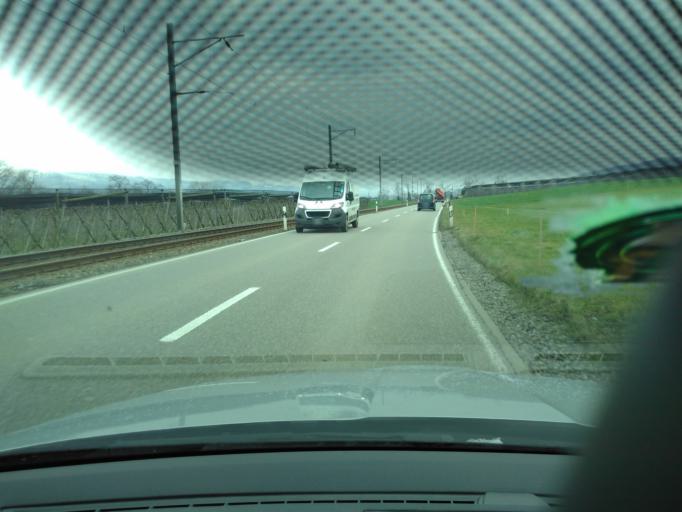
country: CH
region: Lucerne
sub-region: Hochdorf District
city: Hitzkirch
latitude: 47.2022
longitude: 8.2702
